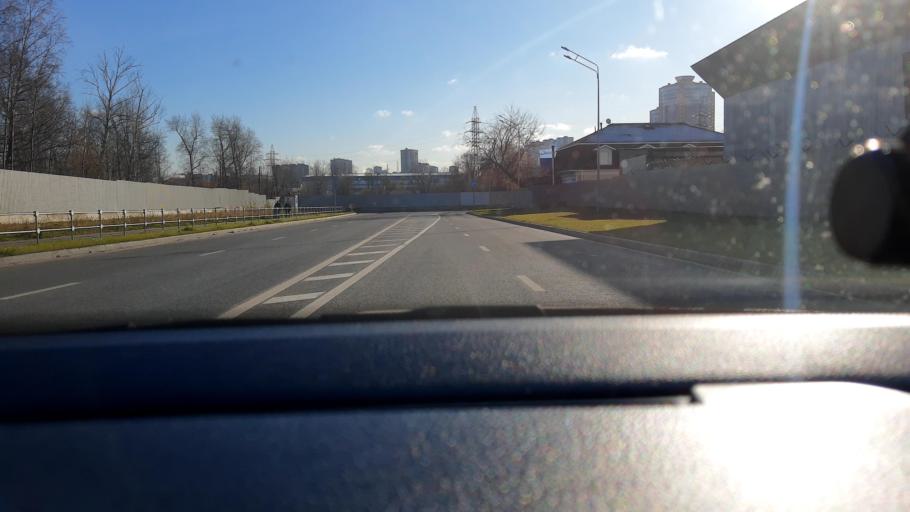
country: RU
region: Moscow
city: Ivanovskoye
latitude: 55.7817
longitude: 37.8474
